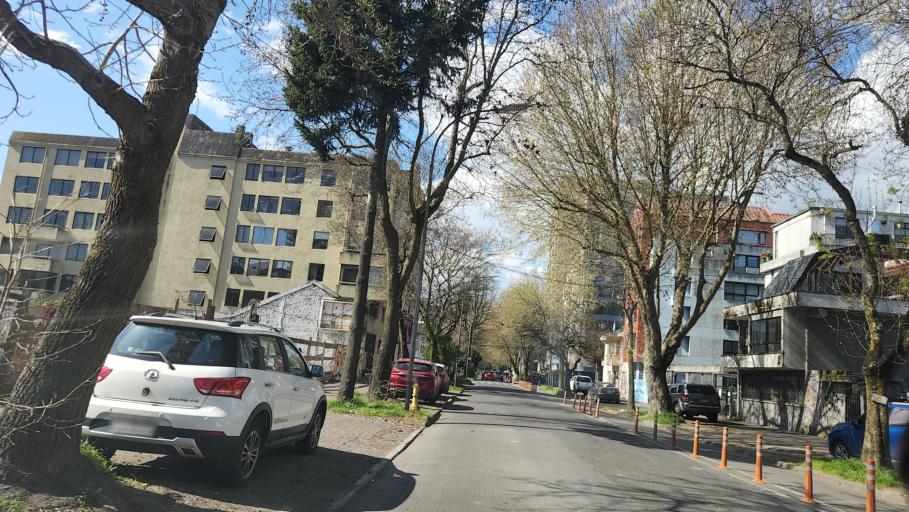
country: CL
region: Biobio
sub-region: Provincia de Concepcion
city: Concepcion
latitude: -36.8218
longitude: -73.0393
